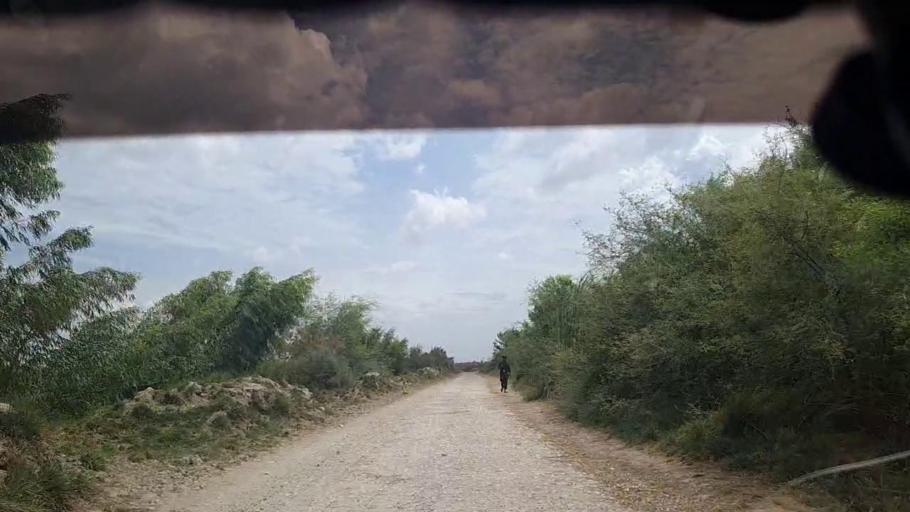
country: PK
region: Sindh
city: Rustam jo Goth
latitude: 28.0462
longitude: 68.9416
